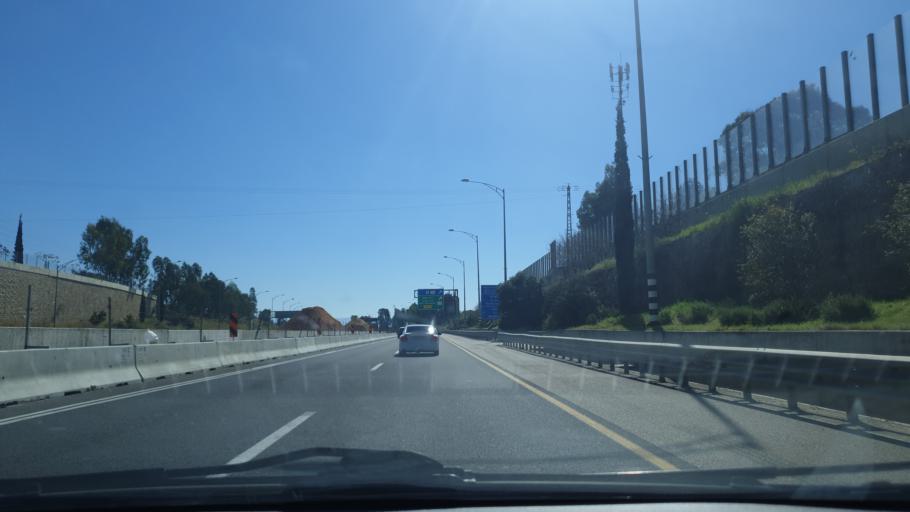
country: IL
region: Central District
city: Ramla
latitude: 31.9121
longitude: 34.8723
